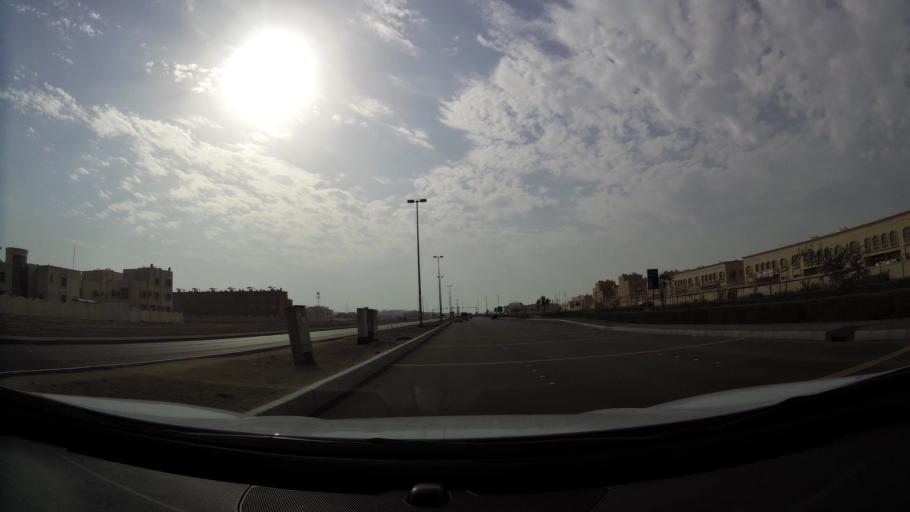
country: AE
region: Abu Dhabi
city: Abu Dhabi
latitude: 24.3480
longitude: 54.5563
